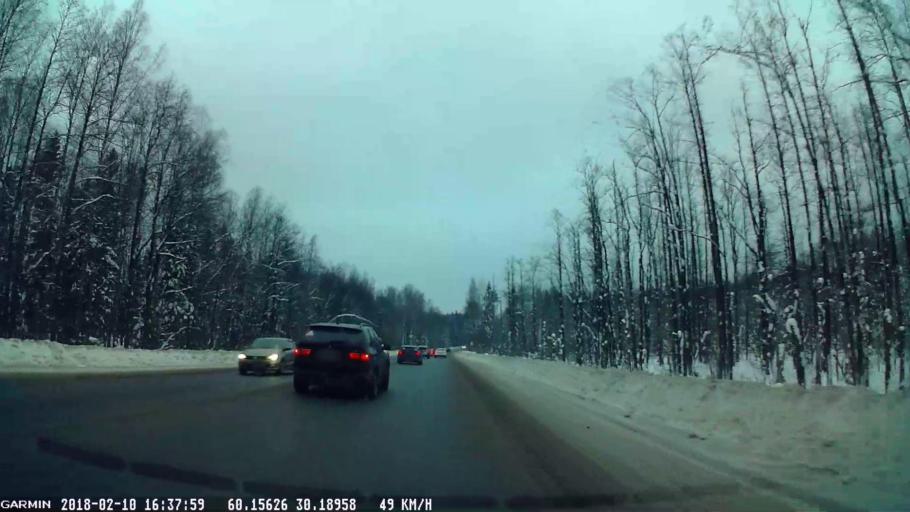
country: RU
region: Leningrad
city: Sertolovo
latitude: 60.1523
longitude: 30.1946
